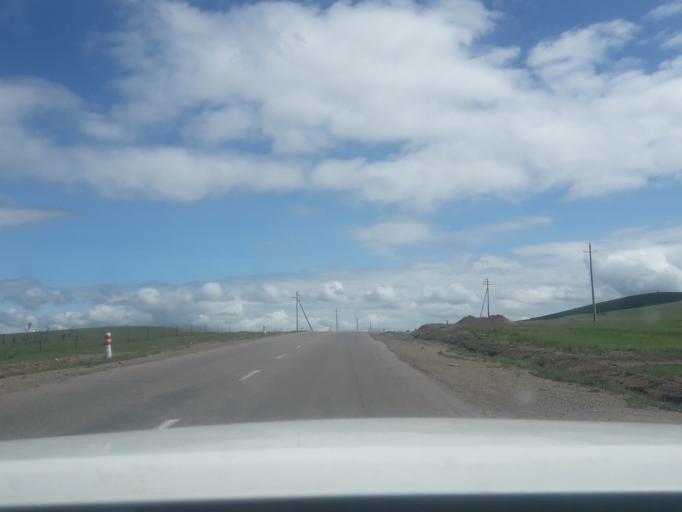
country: MN
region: Central Aimak
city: Altanbulag
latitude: 47.9012
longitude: 106.4924
